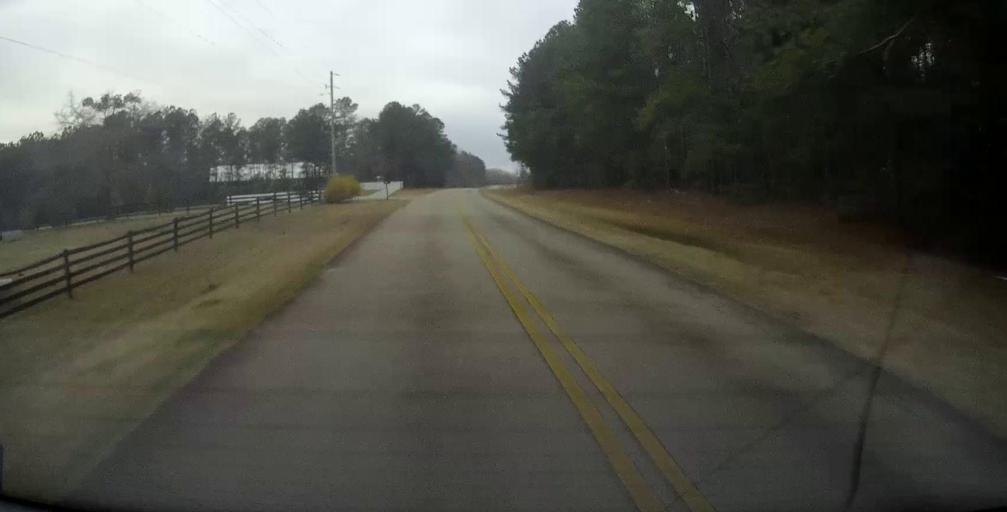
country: US
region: Georgia
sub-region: Monroe County
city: Forsyth
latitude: 32.9761
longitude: -83.9991
